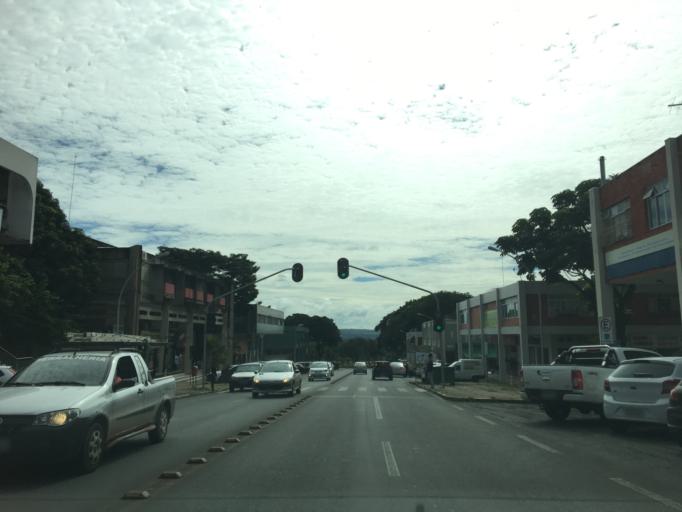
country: BR
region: Federal District
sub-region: Brasilia
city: Brasilia
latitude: -15.7504
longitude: -47.8935
